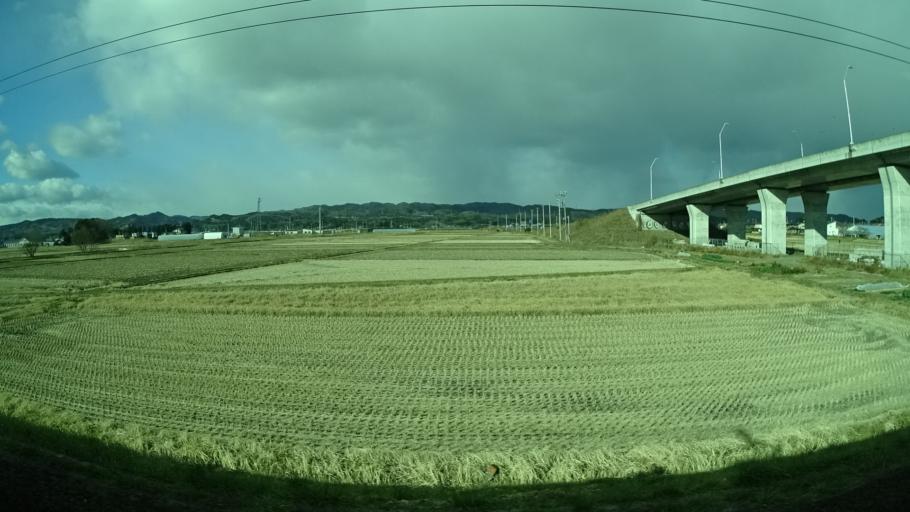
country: JP
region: Miyagi
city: Iwanuma
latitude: 38.1399
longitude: 140.8787
